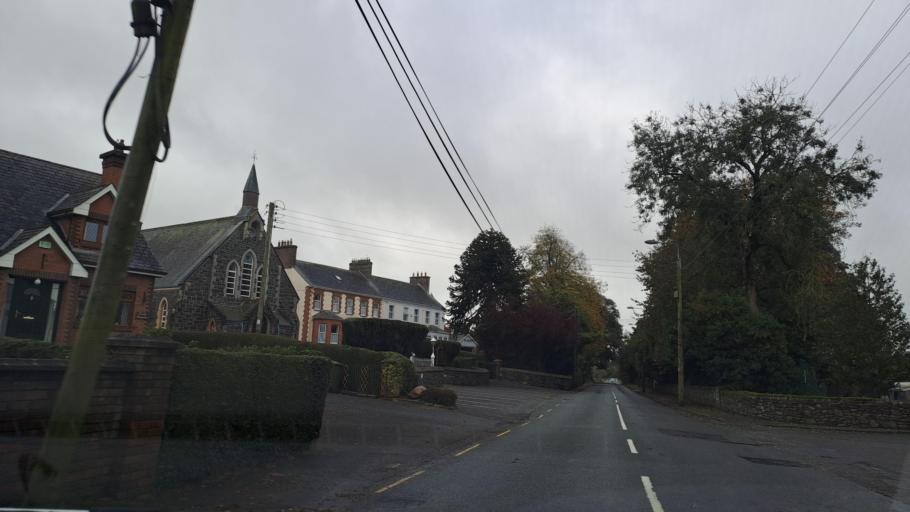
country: IE
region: Ulster
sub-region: An Cabhan
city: Bailieborough
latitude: 53.9137
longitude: -6.9713
